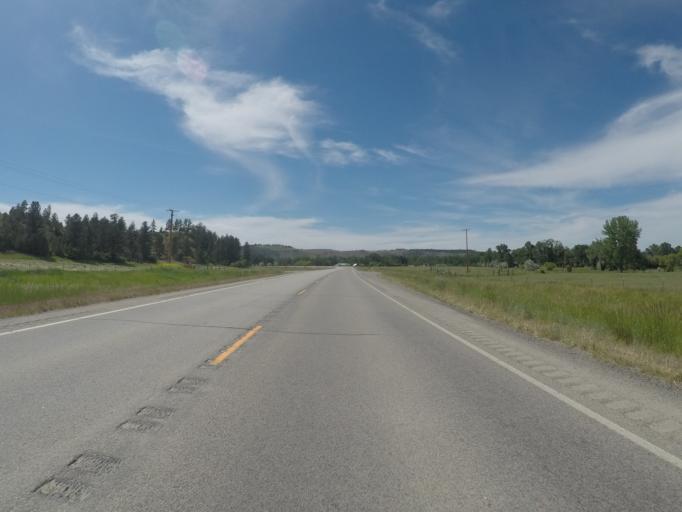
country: US
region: Montana
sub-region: Stillwater County
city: Columbus
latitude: 45.6303
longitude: -109.2685
